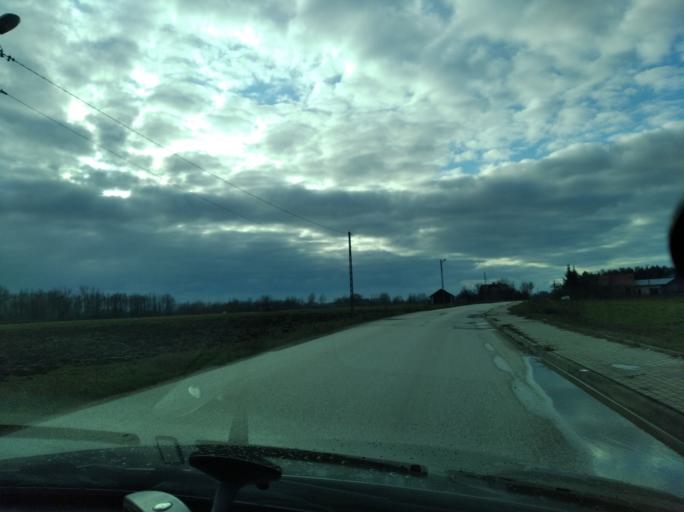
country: PL
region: Subcarpathian Voivodeship
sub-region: Powiat lancucki
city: Czarna
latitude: 50.1139
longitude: 22.2217
